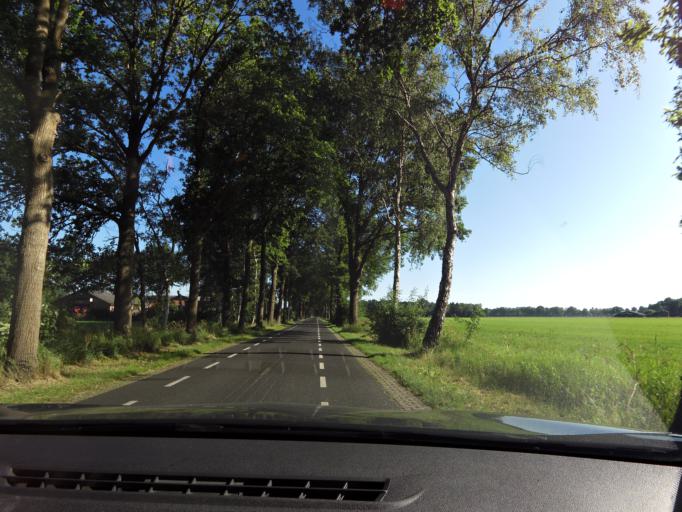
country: NL
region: Gelderland
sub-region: Gemeente Lochem
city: Harfsen
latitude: 52.2919
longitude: 6.3055
